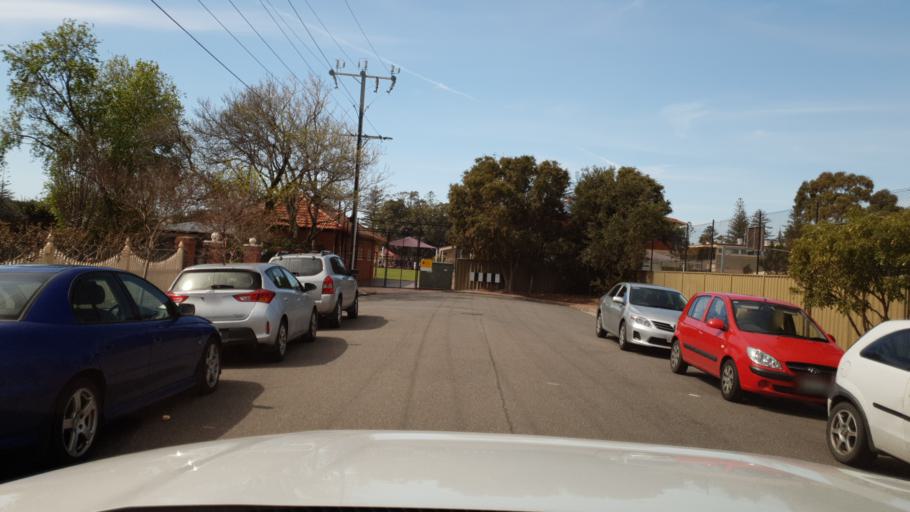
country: AU
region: South Australia
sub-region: Adelaide
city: Glenelg
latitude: -34.9842
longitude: 138.5152
